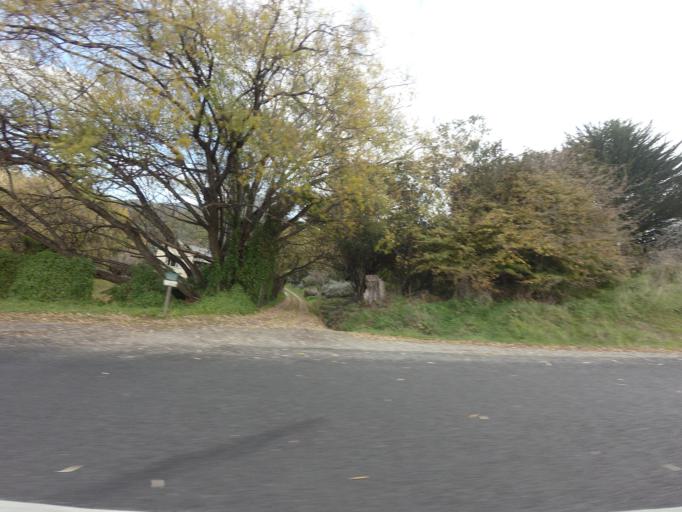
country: AU
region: Tasmania
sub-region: Meander Valley
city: Deloraine
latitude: -41.6275
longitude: 146.7049
